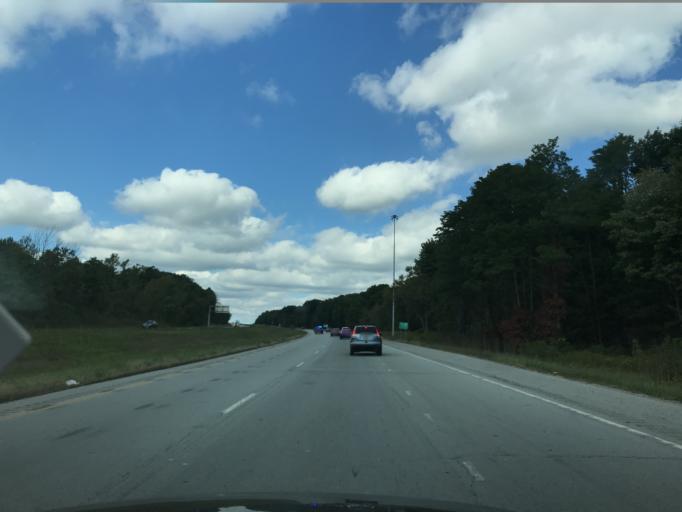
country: US
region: Ohio
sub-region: Summit County
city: Twinsburg
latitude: 41.3149
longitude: -81.4544
